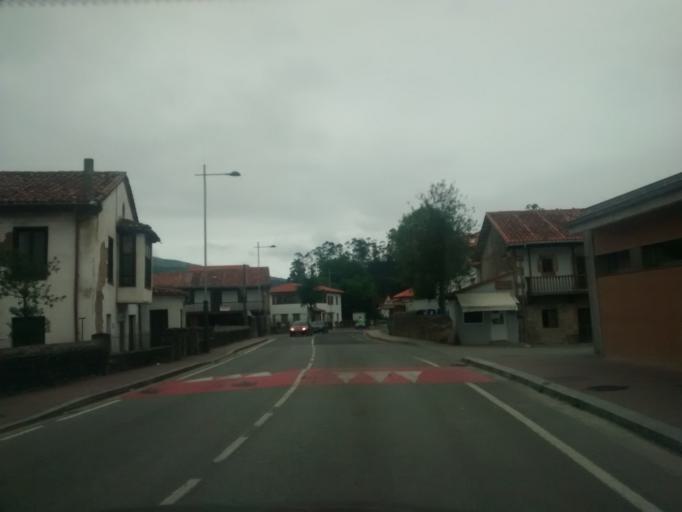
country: ES
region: Cantabria
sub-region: Provincia de Cantabria
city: Luzmela
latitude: 43.3175
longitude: -4.1915
